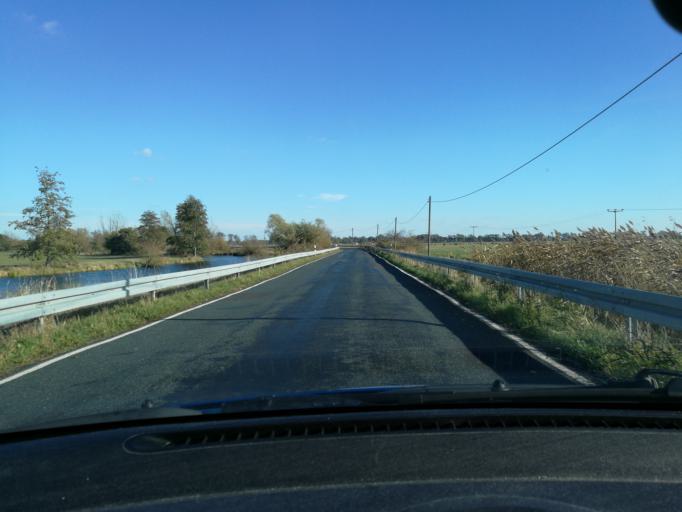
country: DE
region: Lower Saxony
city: Gorleben
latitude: 53.1084
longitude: 11.3934
